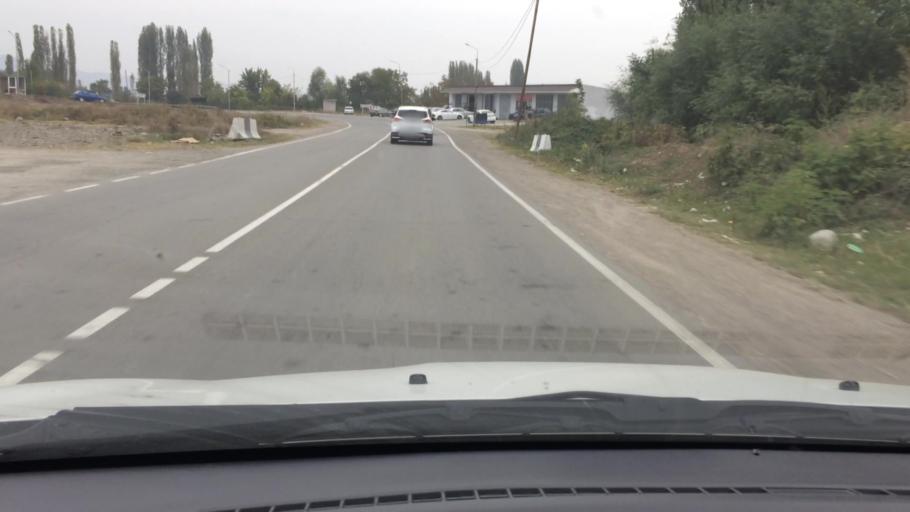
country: AM
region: Tavush
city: Bagratashen
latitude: 41.2532
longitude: 44.7998
